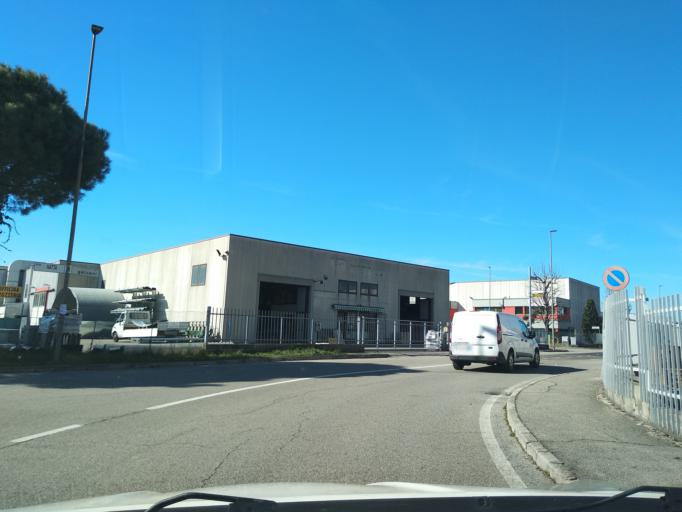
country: IT
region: Veneto
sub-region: Provincia di Padova
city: Rubano
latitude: 45.4212
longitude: 11.7926
